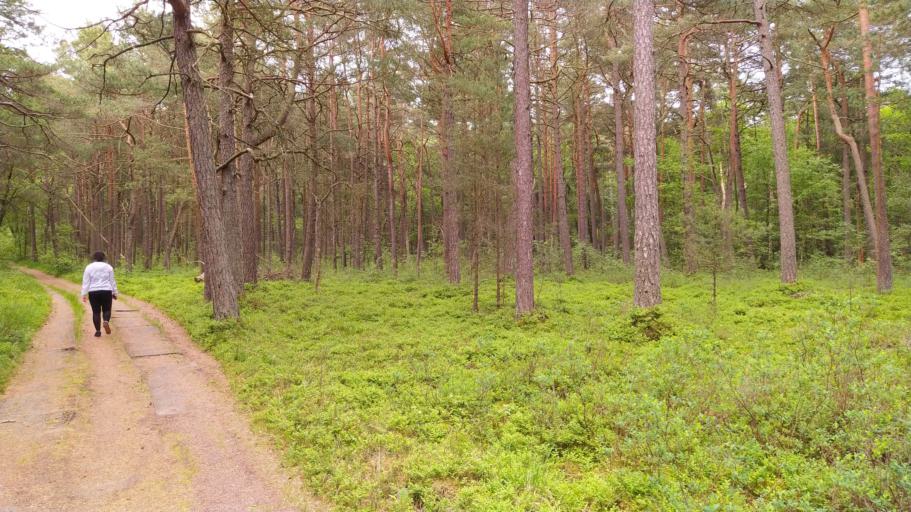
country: PL
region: Pomeranian Voivodeship
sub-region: Powiat slupski
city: Smoldzino
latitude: 54.6908
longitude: 17.1557
